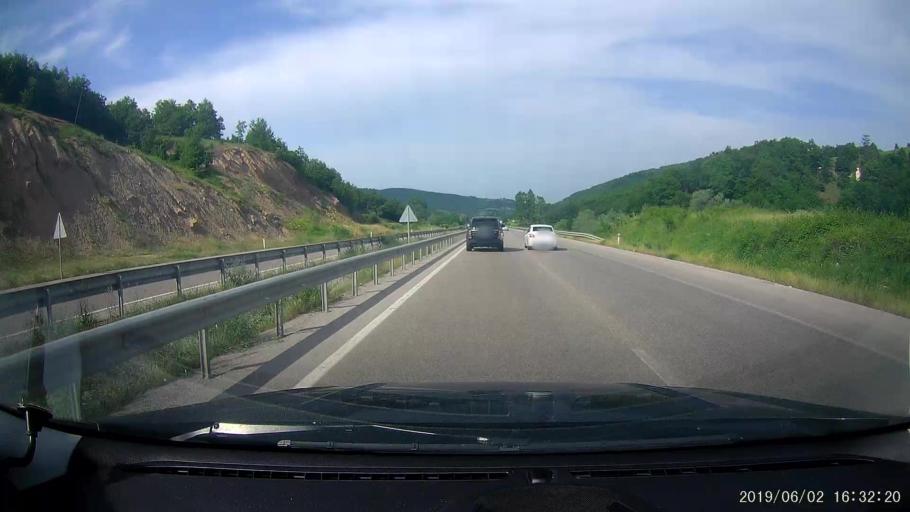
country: TR
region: Samsun
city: Kavak
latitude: 41.0388
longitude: 35.9187
